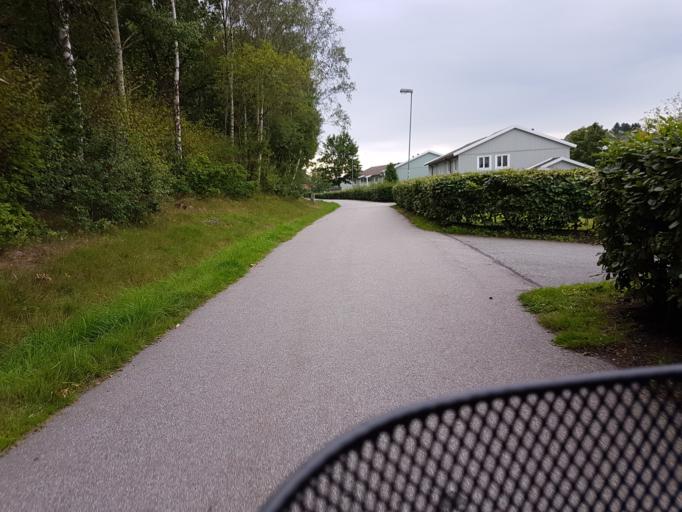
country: SE
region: Vaestra Goetaland
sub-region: Ale Kommun
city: Nodinge-Nol
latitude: 57.9066
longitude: 12.0613
